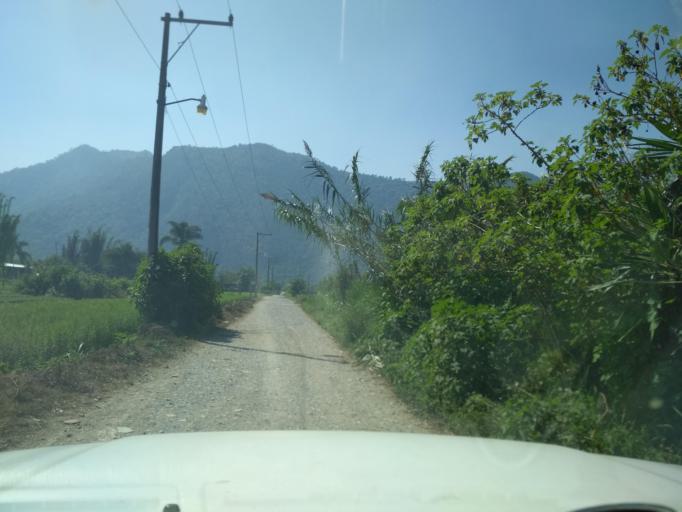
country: MX
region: Veracruz
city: Jalapilla
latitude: 18.8160
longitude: -97.0872
